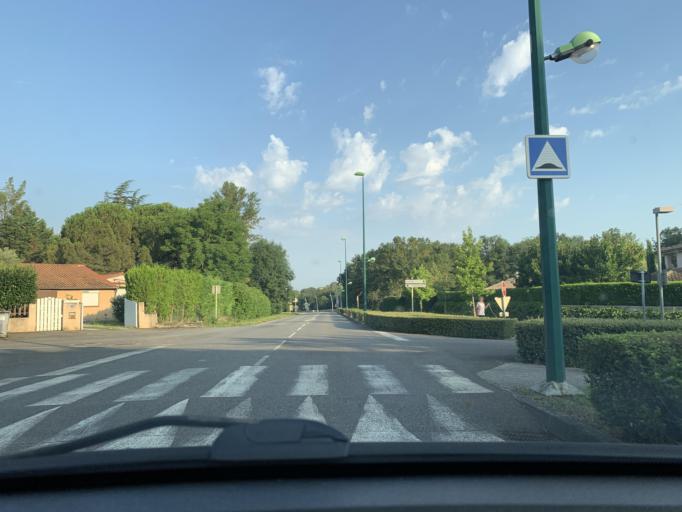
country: FR
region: Midi-Pyrenees
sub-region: Departement de la Haute-Garonne
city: Labege
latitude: 43.5326
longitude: 1.5481
